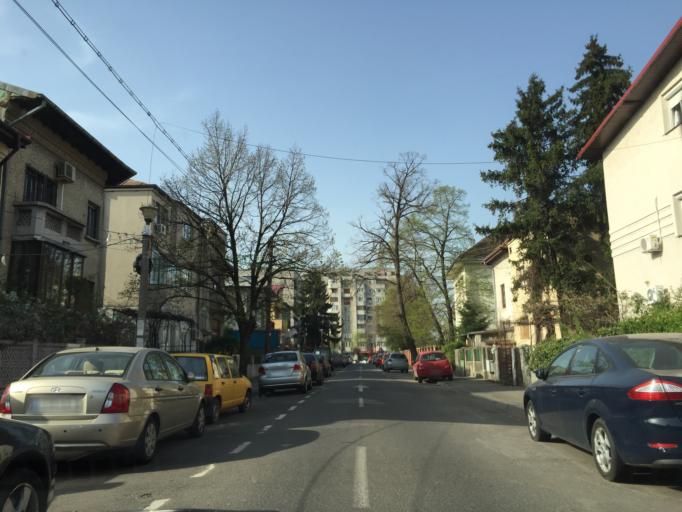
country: RO
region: Bucuresti
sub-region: Municipiul Bucuresti
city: Bucuresti
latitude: 44.4277
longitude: 26.0693
